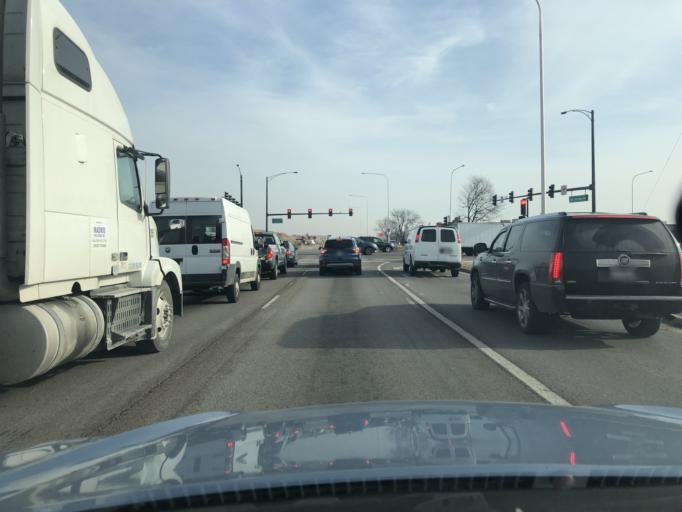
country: US
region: Illinois
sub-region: Cook County
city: Elk Grove Village
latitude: 41.9823
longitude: -87.9602
